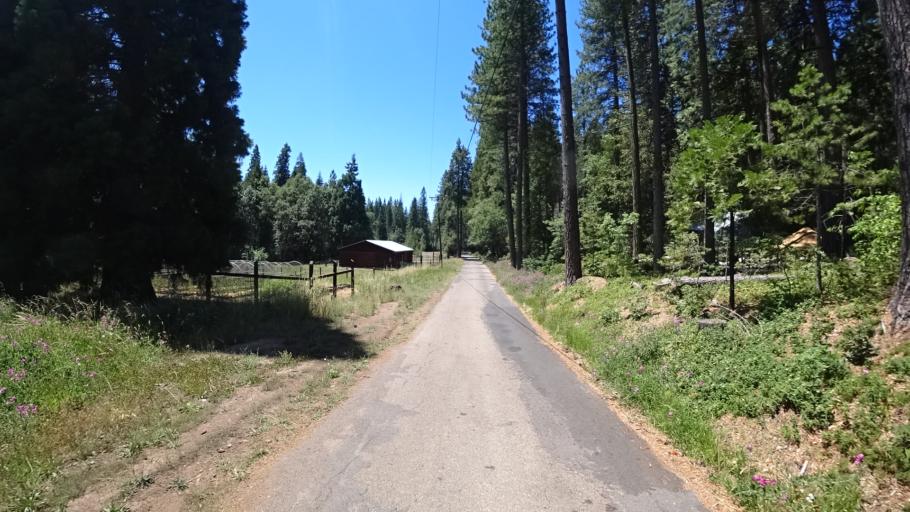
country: US
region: California
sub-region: Calaveras County
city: Arnold
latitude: 38.2428
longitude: -120.3115
